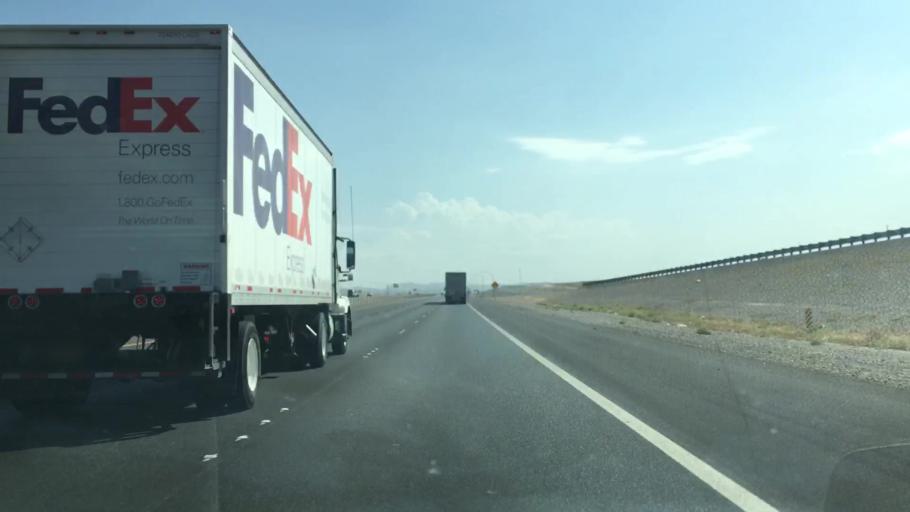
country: US
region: Nevada
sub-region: Clark County
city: Nellis Air Force Base
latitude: 36.2709
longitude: -115.0554
